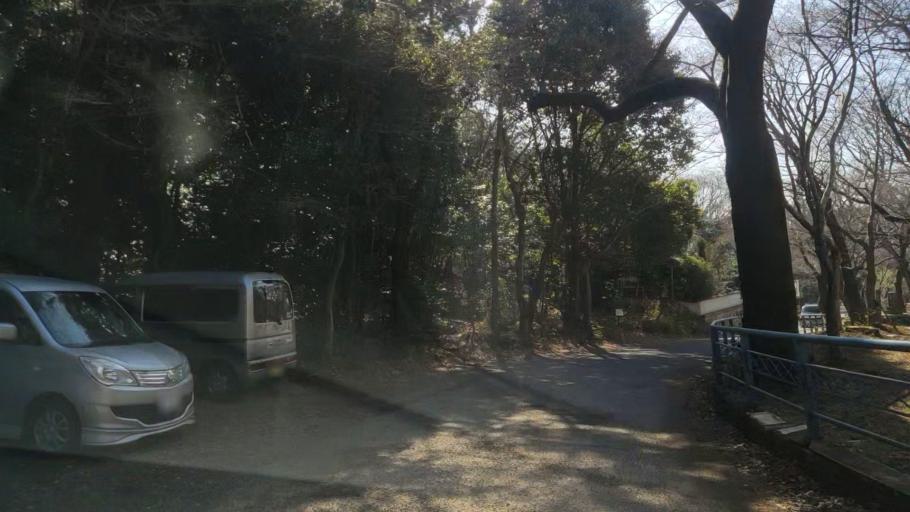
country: JP
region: Gifu
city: Gifu-shi
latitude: 35.4273
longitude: 136.7832
